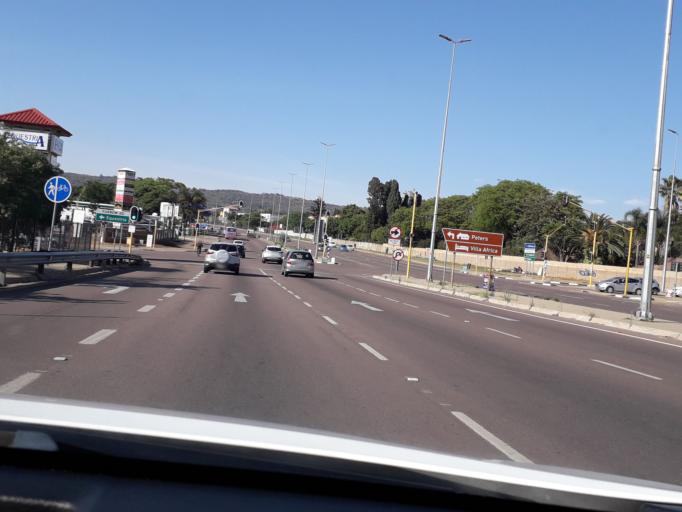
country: ZA
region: Gauteng
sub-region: City of Tshwane Metropolitan Municipality
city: Pretoria
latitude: -25.7535
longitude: 28.3249
